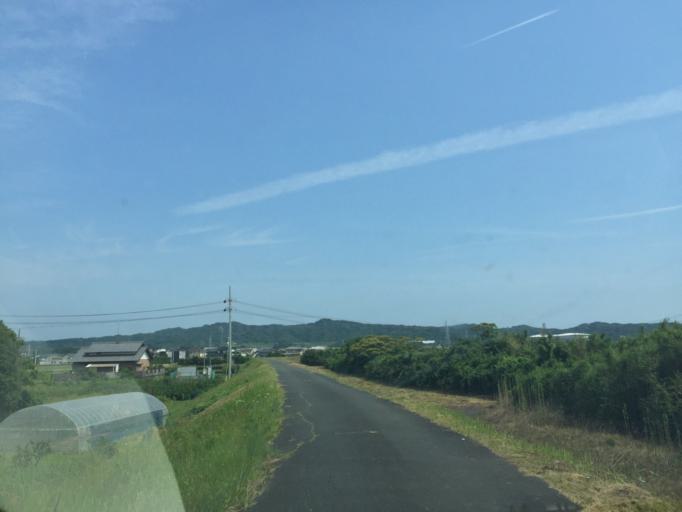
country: JP
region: Shizuoka
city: Fukuroi
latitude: 34.7674
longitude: 137.9605
